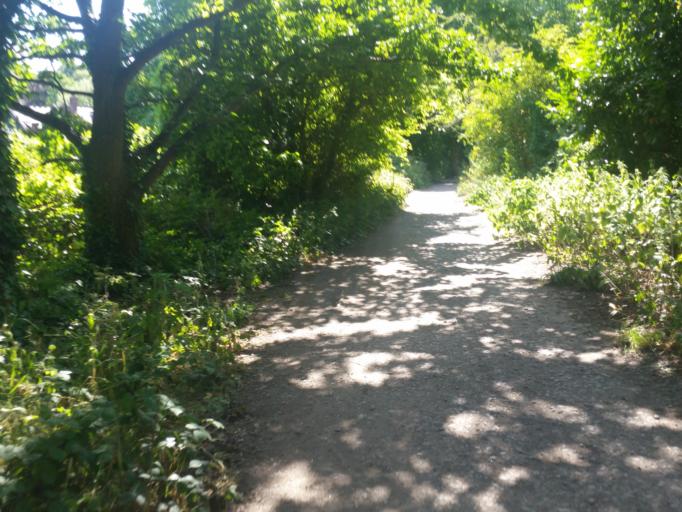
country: GB
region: England
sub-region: Greater London
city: Crouch End
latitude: 51.5869
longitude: -0.1447
